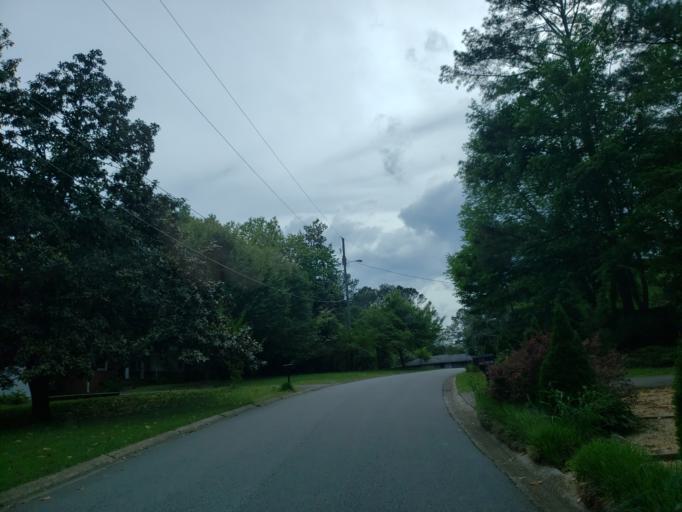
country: US
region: Georgia
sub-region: Cobb County
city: Marietta
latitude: 33.9496
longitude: -84.5673
